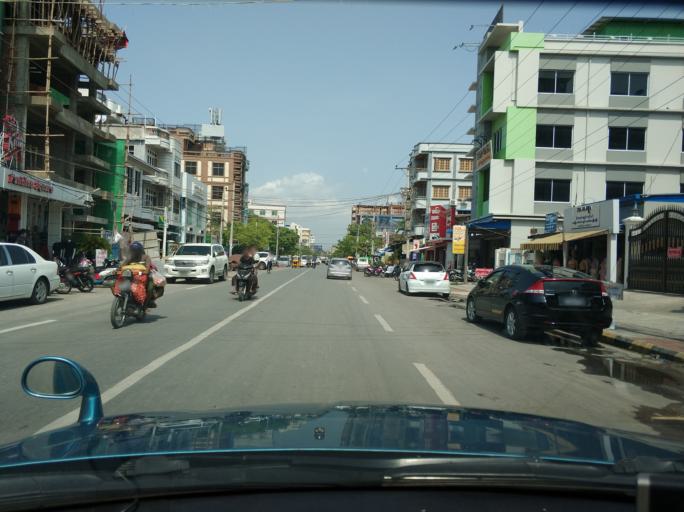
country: MM
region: Mandalay
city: Mandalay
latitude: 21.9659
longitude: 96.0911
